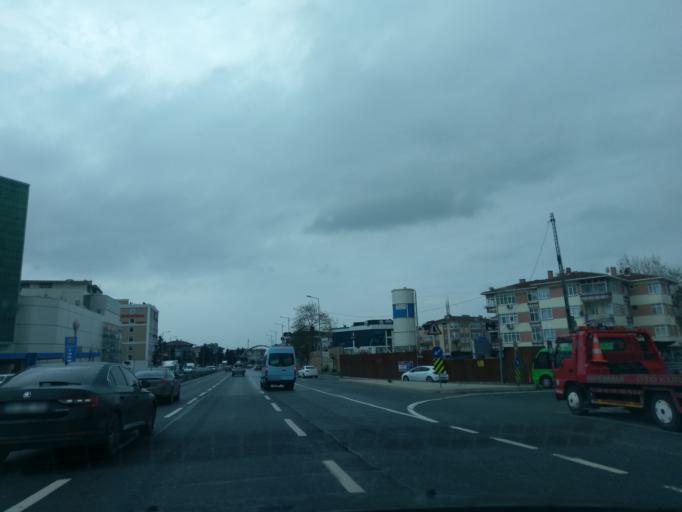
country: TR
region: Istanbul
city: Bueyuekcekmece
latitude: 41.0229
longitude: 28.5848
